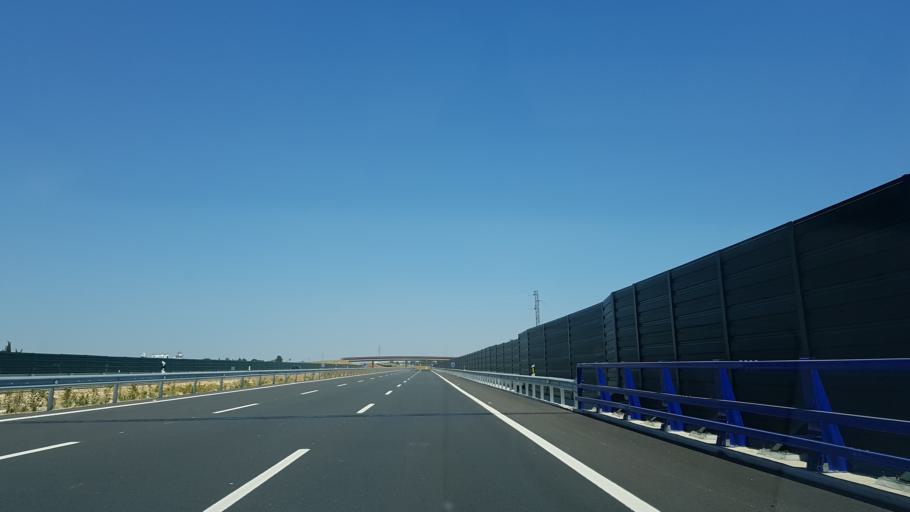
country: ES
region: Andalusia
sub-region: Provincia de Sevilla
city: Coria del Rio
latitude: 37.2969
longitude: -6.0737
